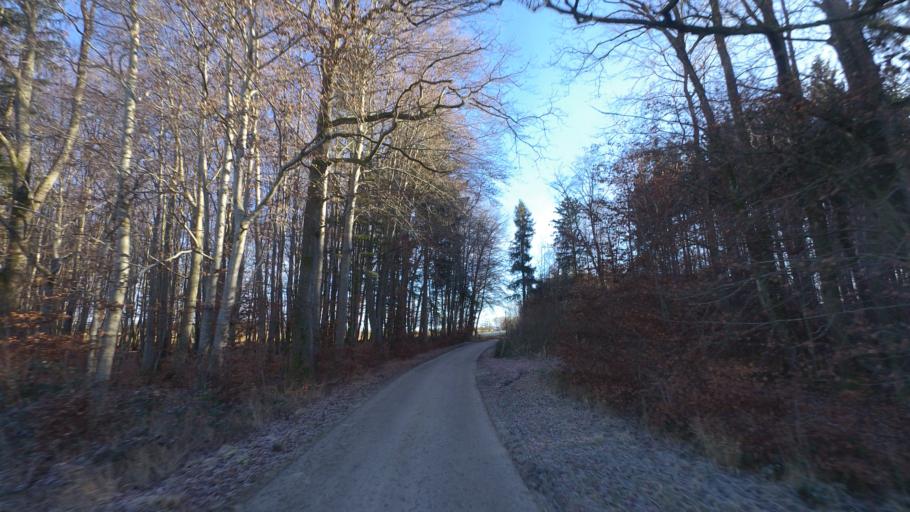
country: DE
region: Bavaria
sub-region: Upper Bavaria
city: Grabenstatt
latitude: 47.8564
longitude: 12.5456
